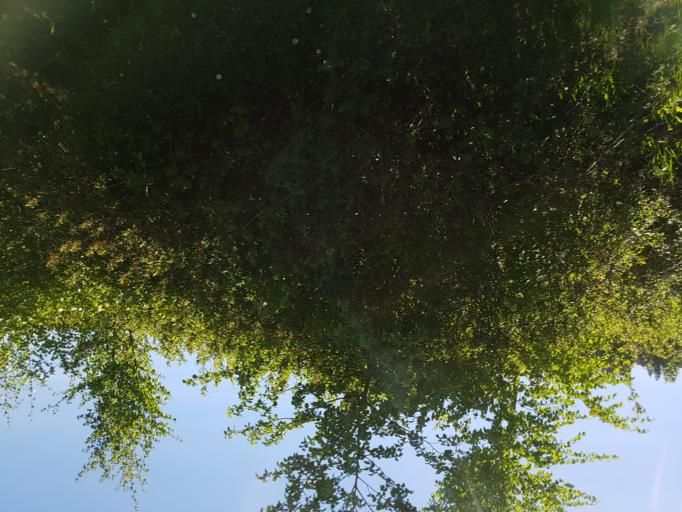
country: NO
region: Sor-Trondelag
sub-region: Klaebu
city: Klaebu
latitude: 63.4220
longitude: 10.5271
